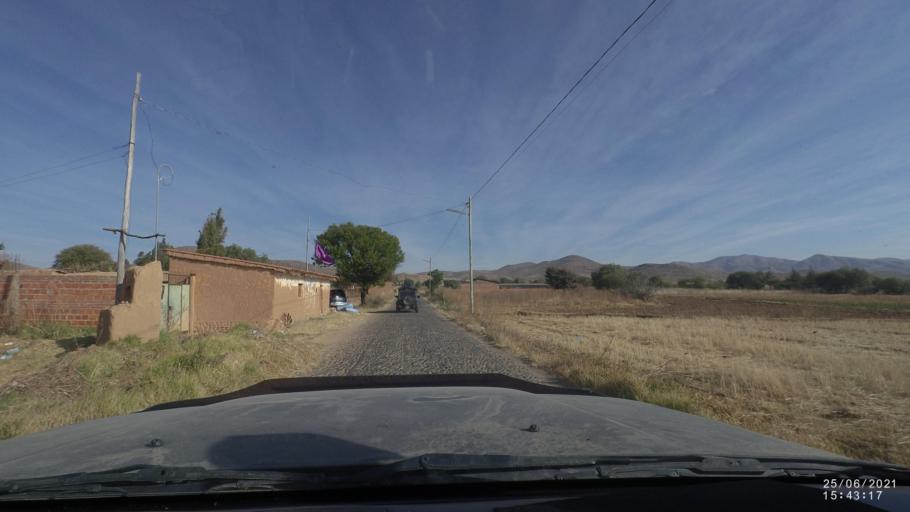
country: BO
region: Cochabamba
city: Cliza
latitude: -17.6467
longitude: -65.9122
